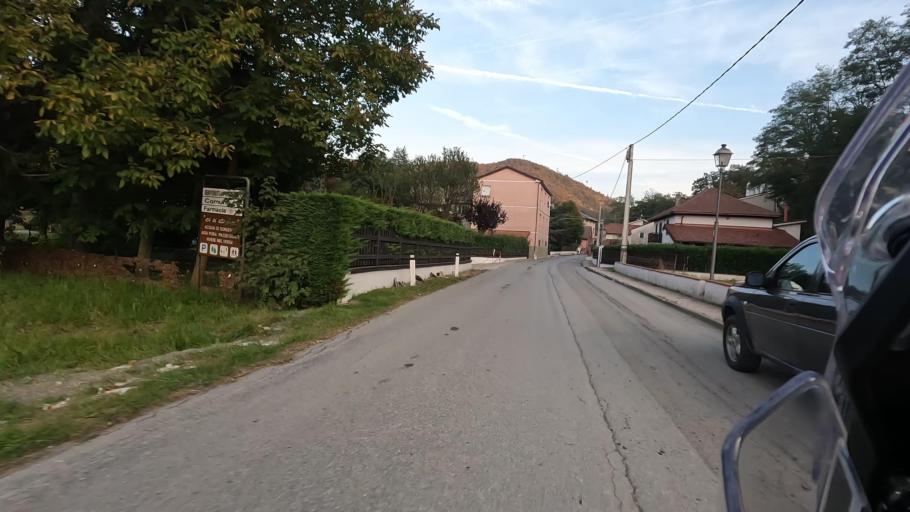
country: IT
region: Liguria
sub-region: Provincia di Savona
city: Pontinvrea
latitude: 44.4461
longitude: 8.4319
